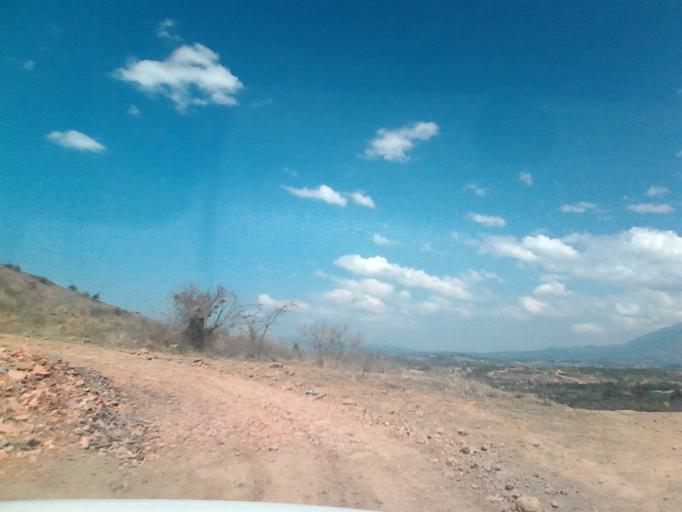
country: CO
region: Boyaca
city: Sachica
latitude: 5.6050
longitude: -73.5677
